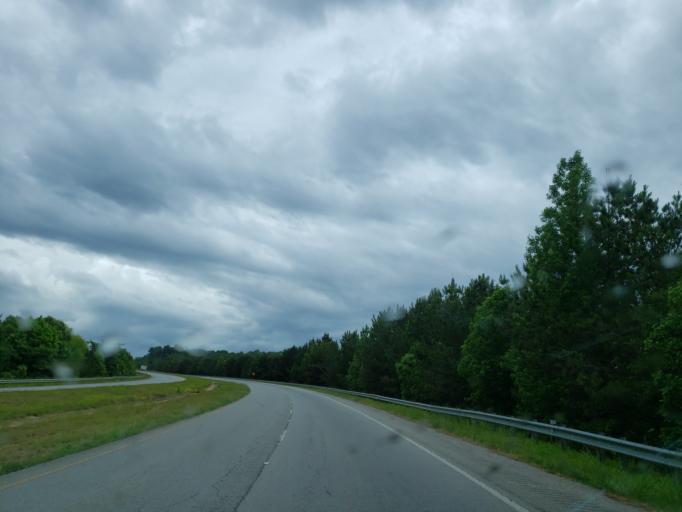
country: US
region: Georgia
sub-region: Haralson County
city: Buchanan
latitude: 33.9150
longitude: -85.2455
